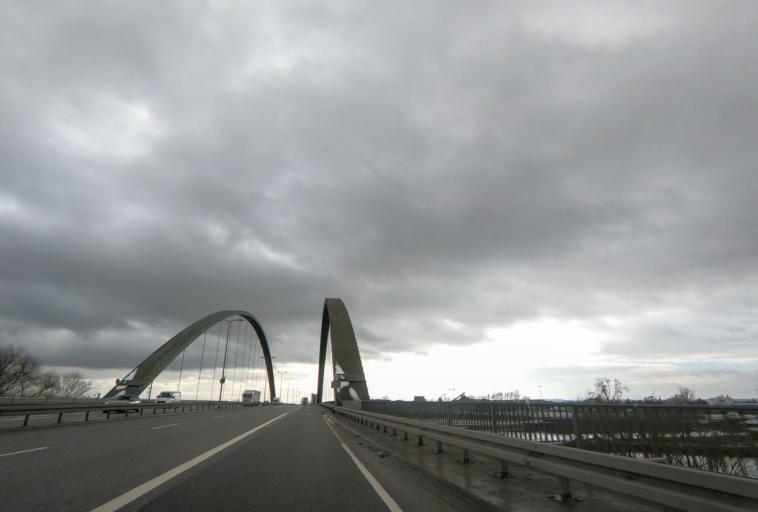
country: DE
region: Bavaria
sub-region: Upper Palatinate
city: Regensburg
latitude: 49.0238
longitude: 12.1398
